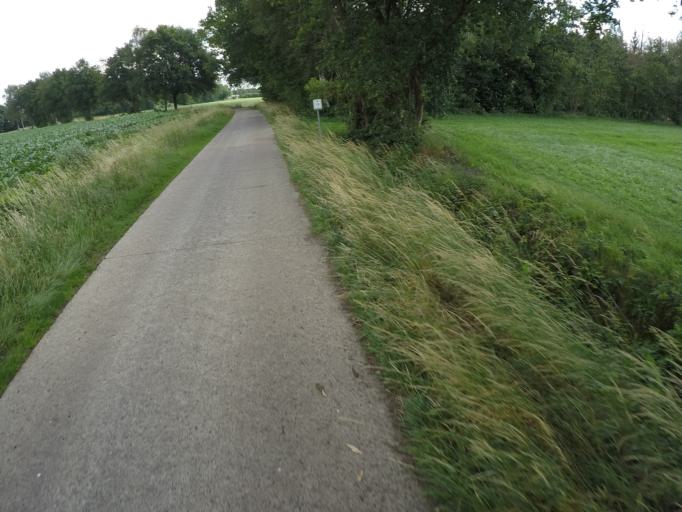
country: BE
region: Flanders
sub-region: Provincie Antwerpen
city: Vosselaar
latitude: 51.2749
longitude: 4.8897
